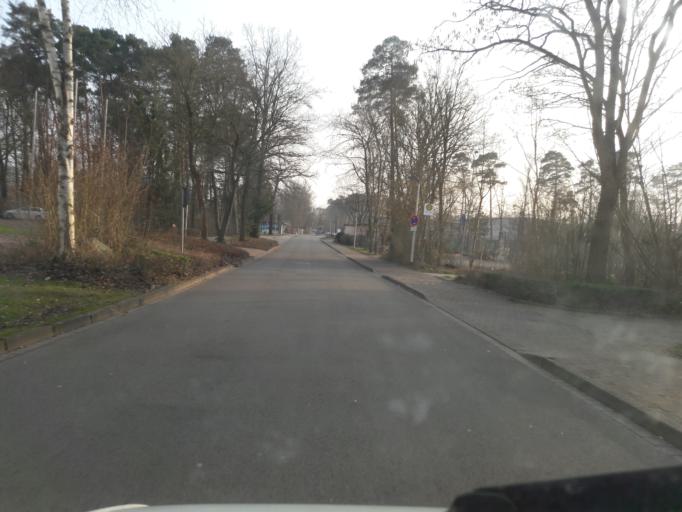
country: DE
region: North Rhine-Westphalia
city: Espelkamp
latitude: 52.3823
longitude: 8.6279
